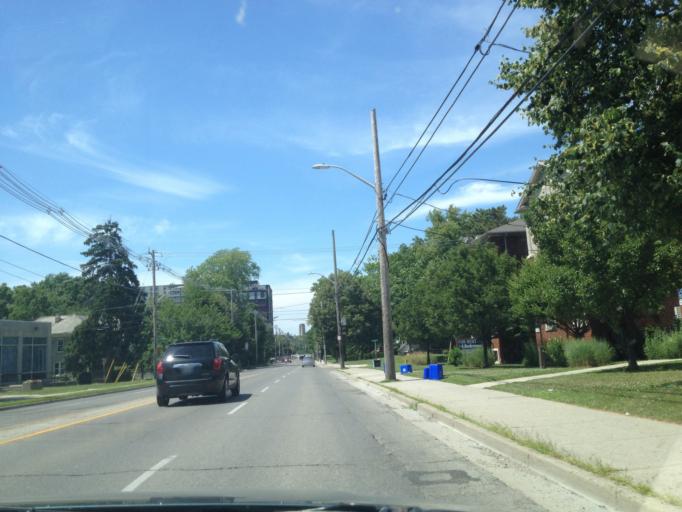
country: CA
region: Ontario
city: London
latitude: 43.0093
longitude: -81.2615
